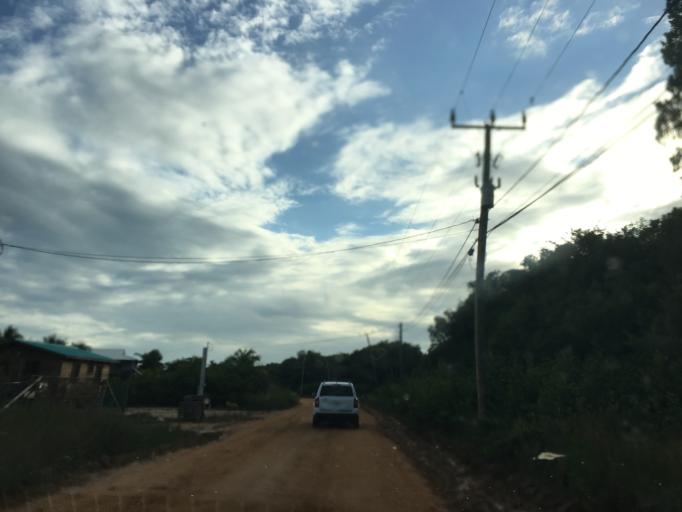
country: BZ
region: Stann Creek
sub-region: Dangriga
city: Dangriga
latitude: 16.8313
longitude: -88.2667
